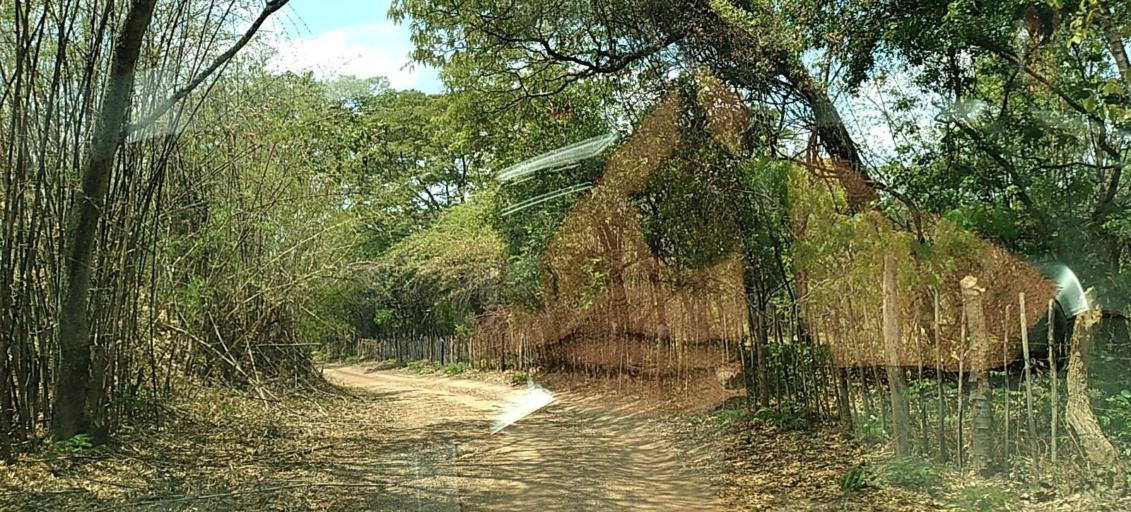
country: ZM
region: Copperbelt
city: Chililabombwe
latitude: -12.4865
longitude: 27.6402
